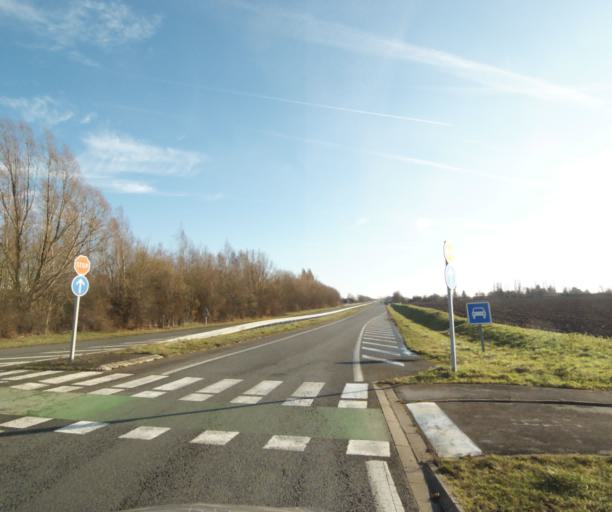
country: FR
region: Nord-Pas-de-Calais
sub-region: Departement du Nord
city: Saultain
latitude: 50.3416
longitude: 3.5838
